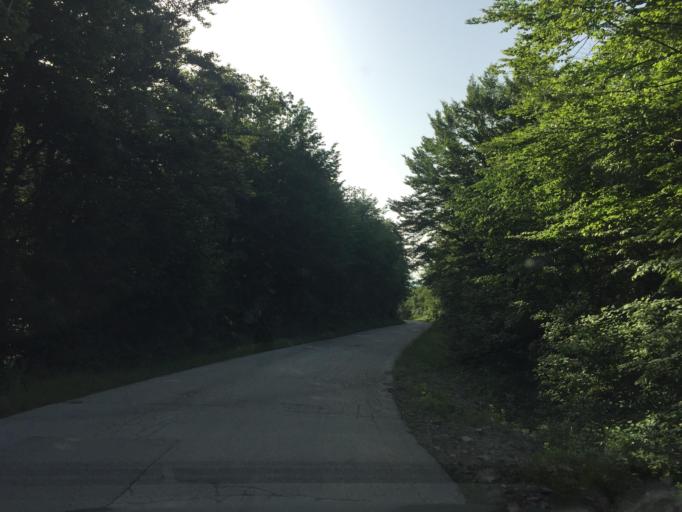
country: HR
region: Istarska
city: Buzet
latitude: 45.4741
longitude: 14.0894
